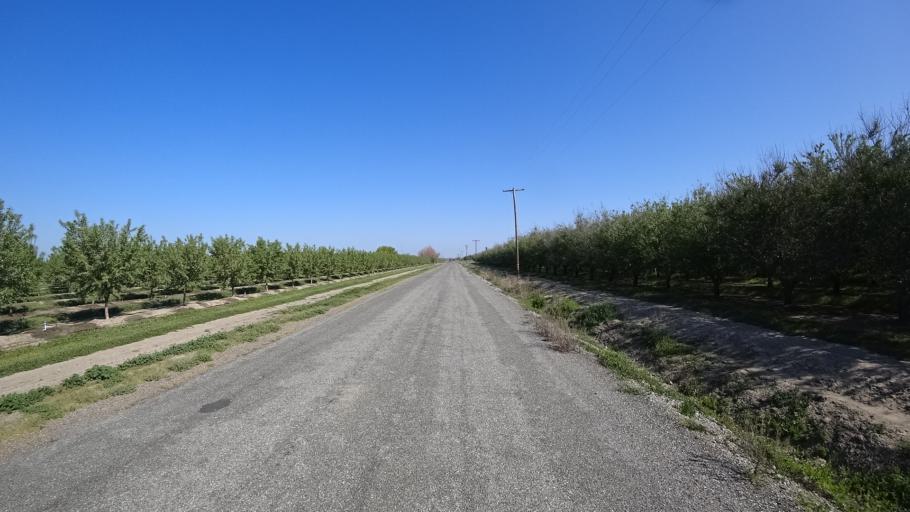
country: US
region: California
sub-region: Glenn County
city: Hamilton City
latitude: 39.6246
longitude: -122.0275
